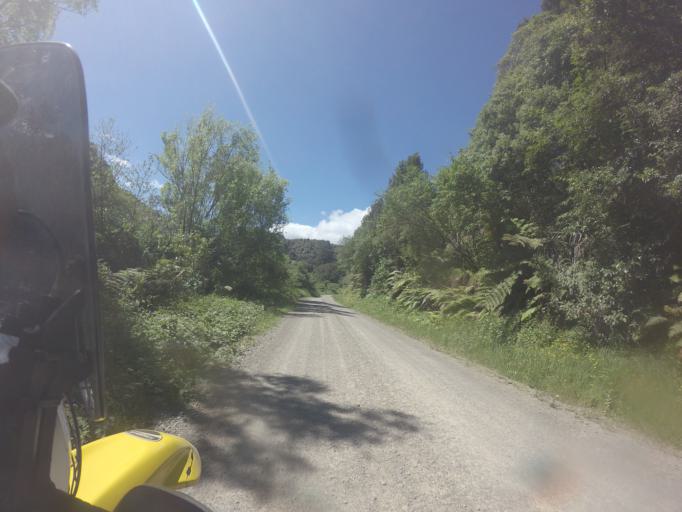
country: NZ
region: Bay of Plenty
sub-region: Opotiki District
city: Opotiki
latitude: -38.2790
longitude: 177.3409
